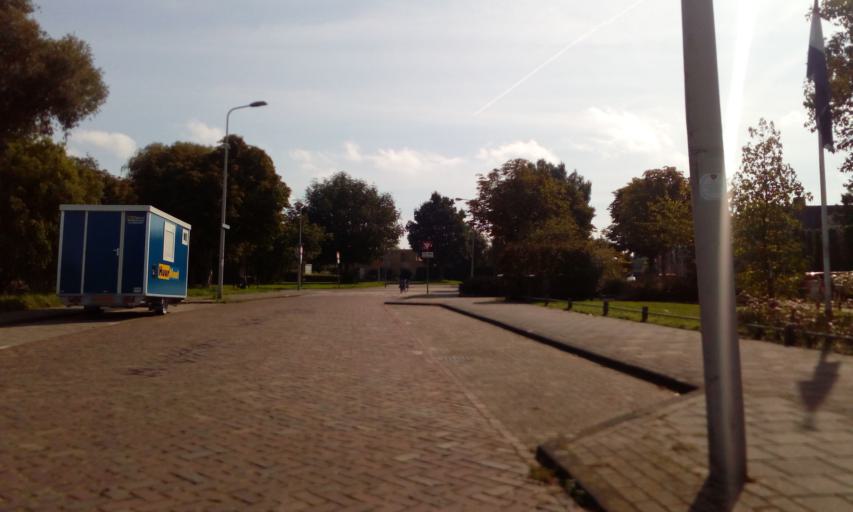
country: NL
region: South Holland
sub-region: Gemeente Oegstgeest
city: Oegstgeest
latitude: 52.1570
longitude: 4.4558
